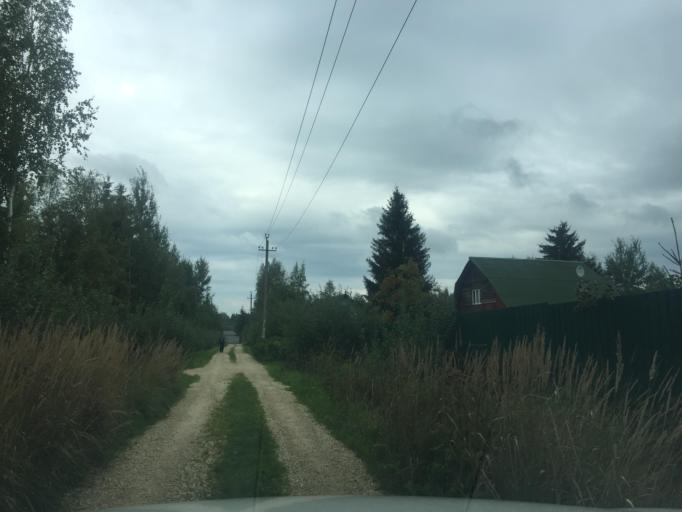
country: RU
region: Leningrad
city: Rozhdestveno
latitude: 59.2967
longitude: 30.0131
